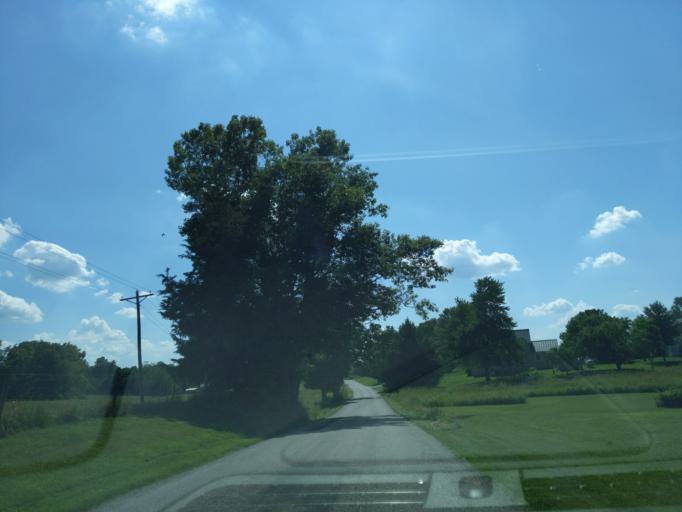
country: US
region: Indiana
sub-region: Ripley County
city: Osgood
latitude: 39.2006
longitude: -85.3758
